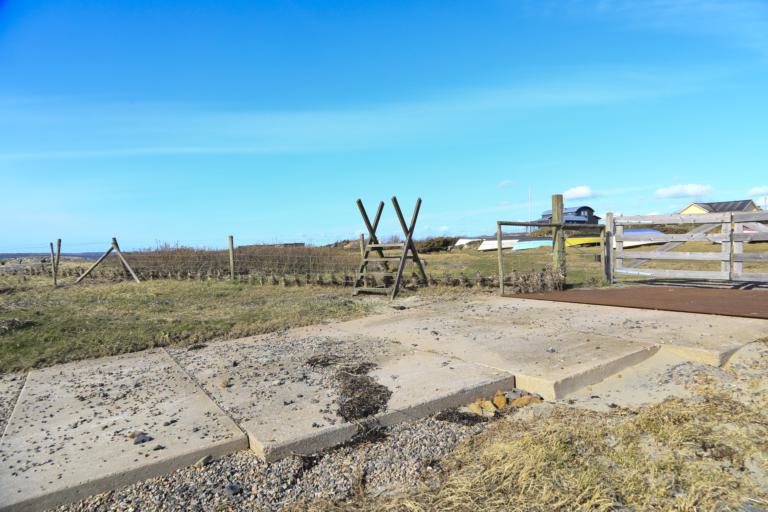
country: SE
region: Halland
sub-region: Varbergs Kommun
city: Varberg
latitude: 57.1225
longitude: 12.2028
